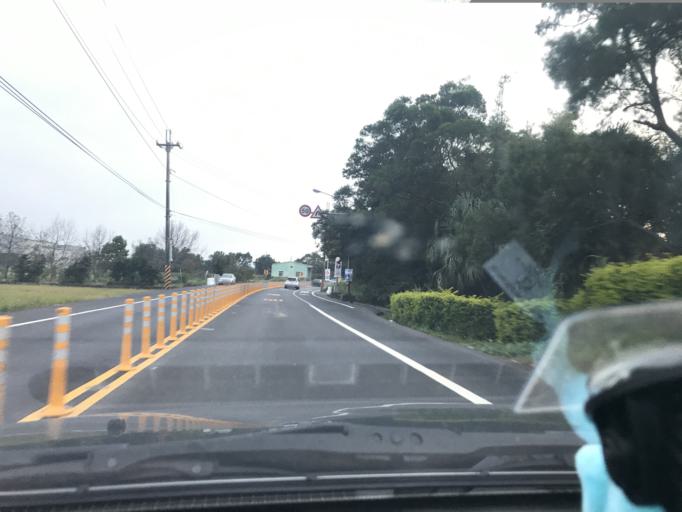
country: TW
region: Taiwan
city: Daxi
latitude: 24.8834
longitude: 121.2214
